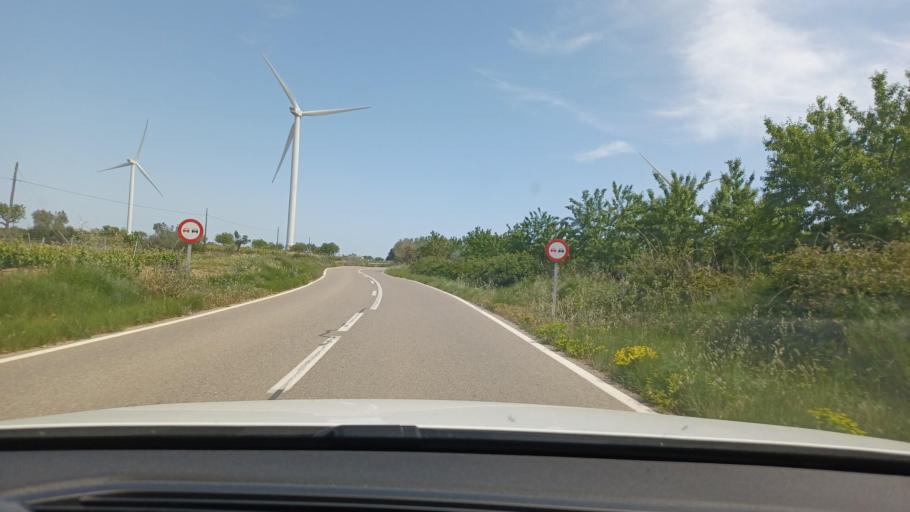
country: ES
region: Catalonia
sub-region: Provincia de Tarragona
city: Vilalba dels Arcs
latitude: 41.1121
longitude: 0.4133
